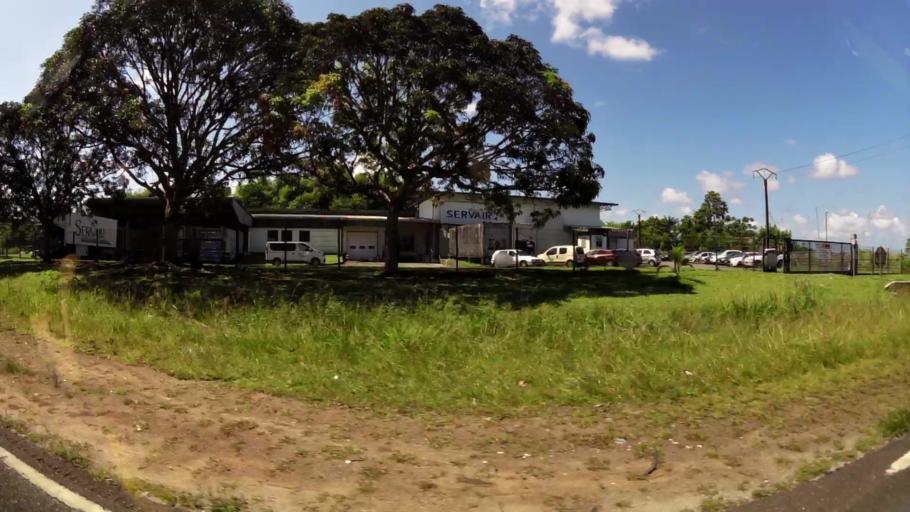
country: GF
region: Guyane
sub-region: Guyane
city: Matoury
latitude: 4.8272
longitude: -52.3597
